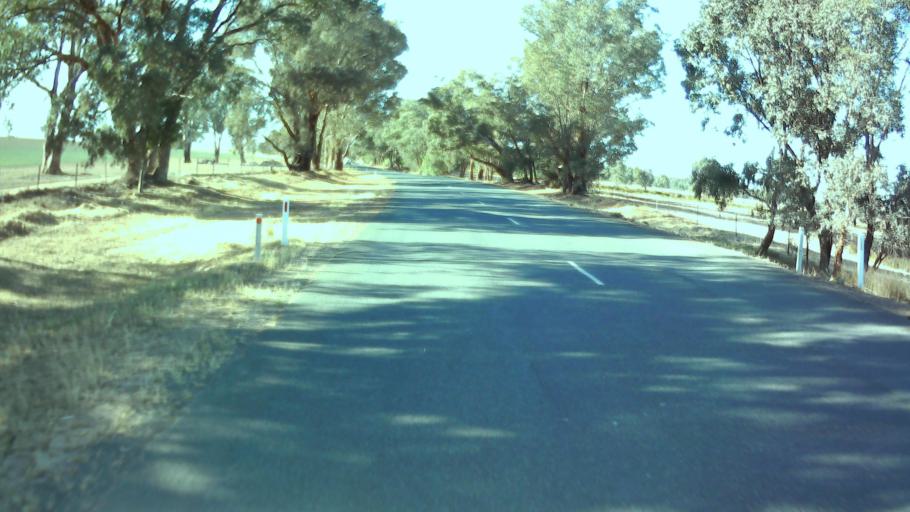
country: AU
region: New South Wales
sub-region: Weddin
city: Grenfell
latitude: -33.9807
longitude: 148.1404
